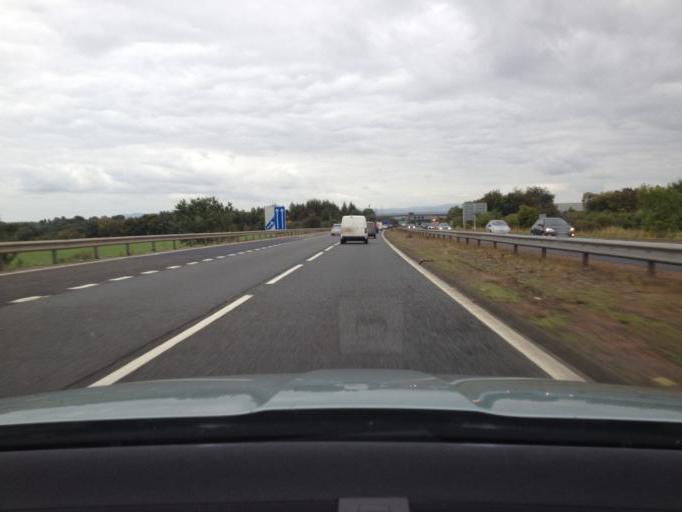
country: GB
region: Scotland
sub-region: Fife
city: Crossgates
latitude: 56.0686
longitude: -3.3874
